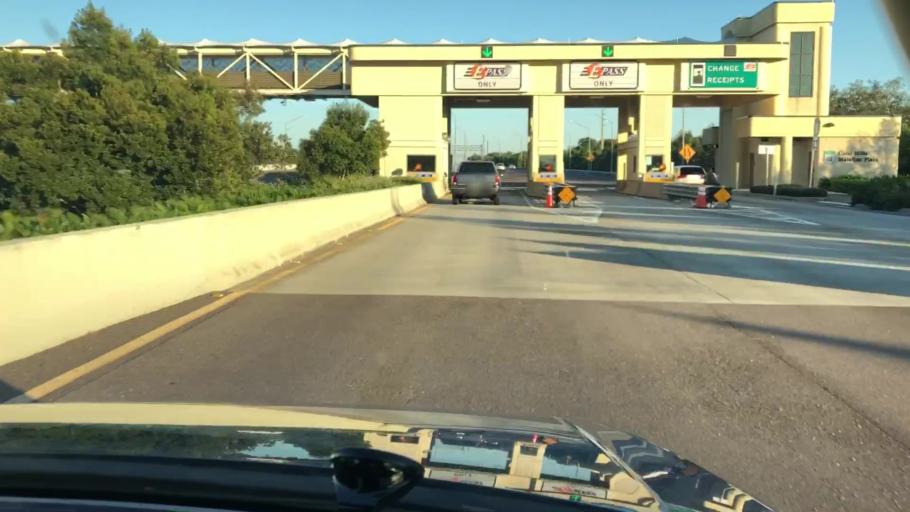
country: US
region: Florida
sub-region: Orange County
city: South Apopka
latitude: 28.6440
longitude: -81.5081
